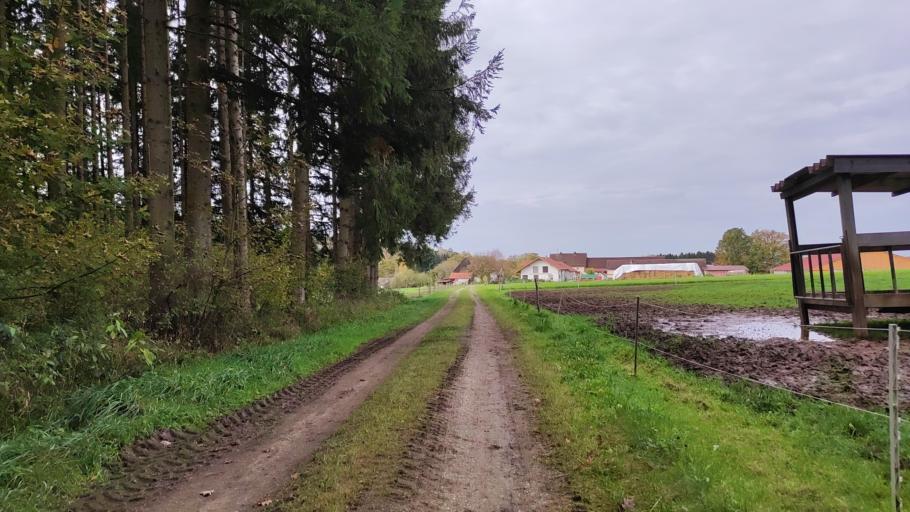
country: DE
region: Bavaria
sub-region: Swabia
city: Munsterhausen
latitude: 48.3168
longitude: 10.4869
